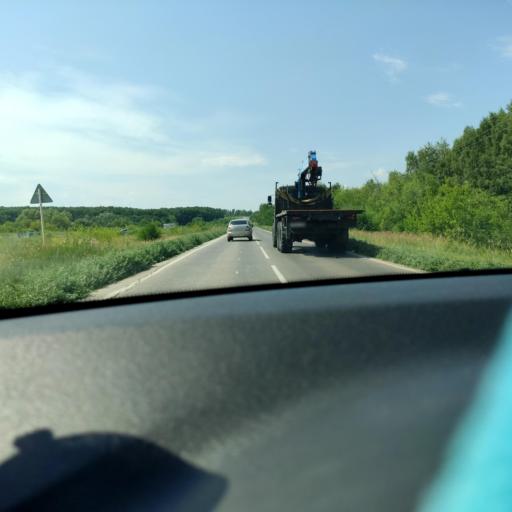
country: RU
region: Samara
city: Petra-Dubrava
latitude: 53.3464
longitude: 50.5079
